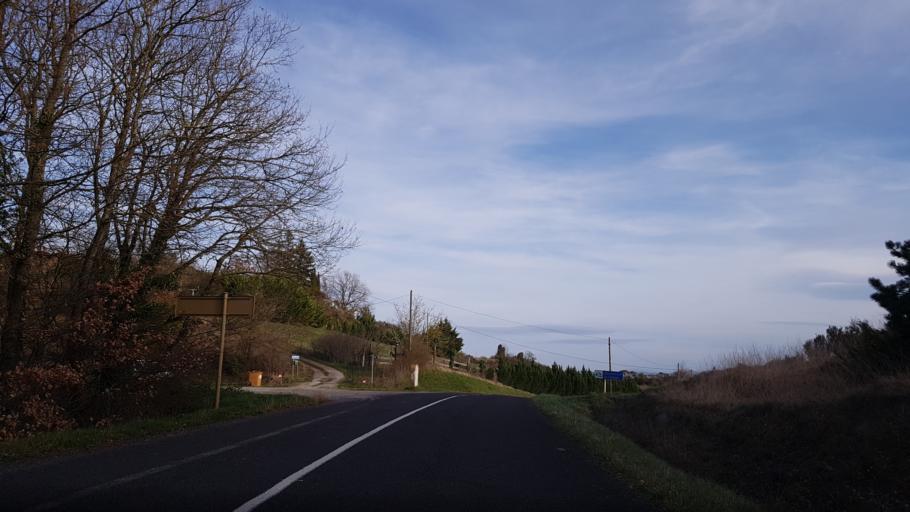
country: FR
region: Midi-Pyrenees
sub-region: Departement de l'Ariege
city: Mirepoix
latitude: 43.1336
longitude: 1.9143
